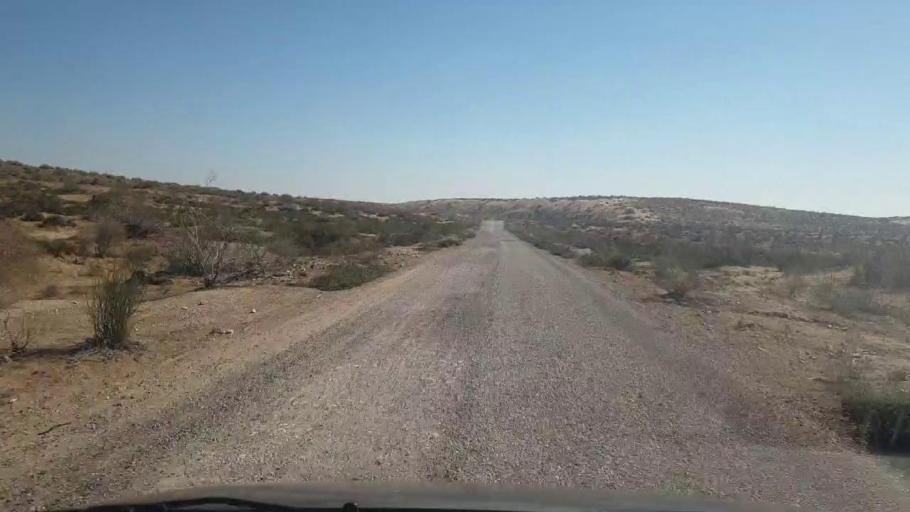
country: PK
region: Sindh
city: Bozdar
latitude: 27.0170
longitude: 68.7348
